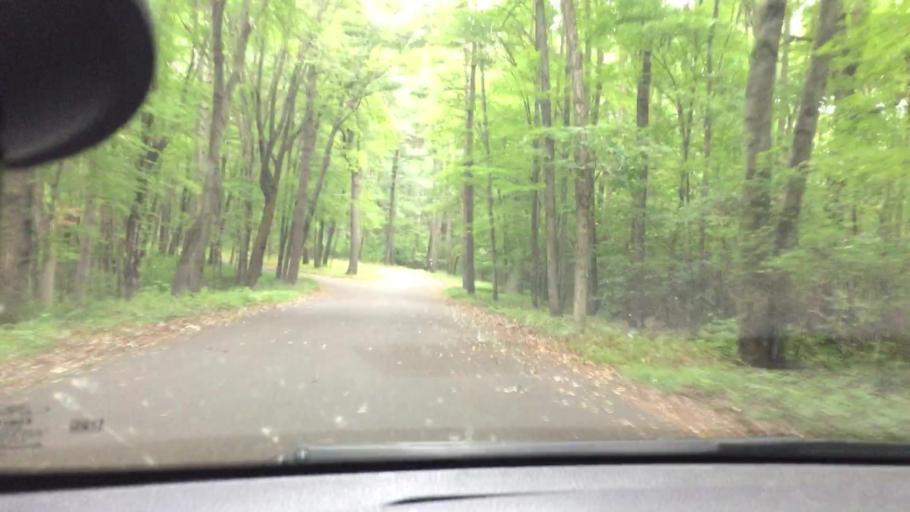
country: US
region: Wisconsin
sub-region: Chippewa County
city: Chippewa Falls
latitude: 44.9601
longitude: -91.4017
